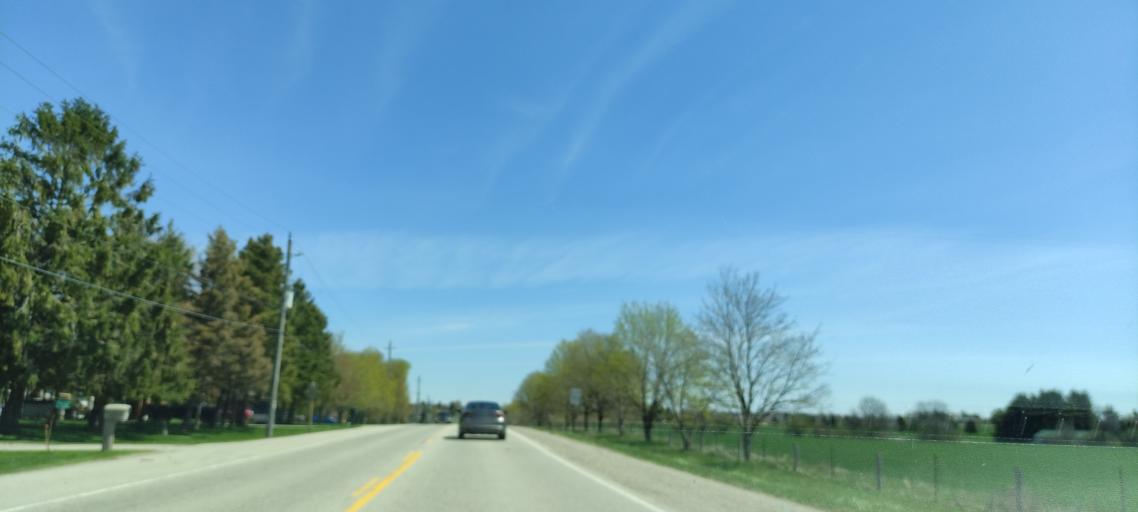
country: CA
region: Ontario
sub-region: Wellington County
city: Guelph
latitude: 43.5997
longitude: -80.3365
